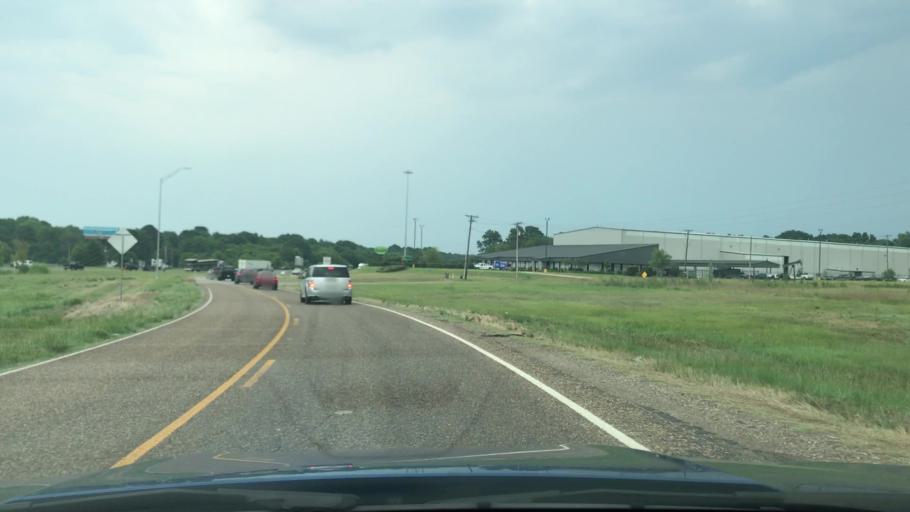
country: US
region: Texas
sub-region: Harrison County
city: Waskom
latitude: 32.4661
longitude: -94.0559
